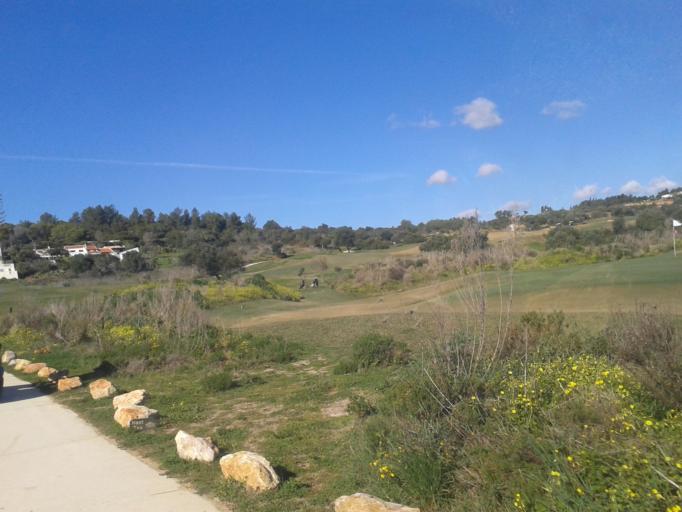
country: PT
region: Faro
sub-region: Lagos
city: Lagos
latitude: 37.1212
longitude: -8.6446
